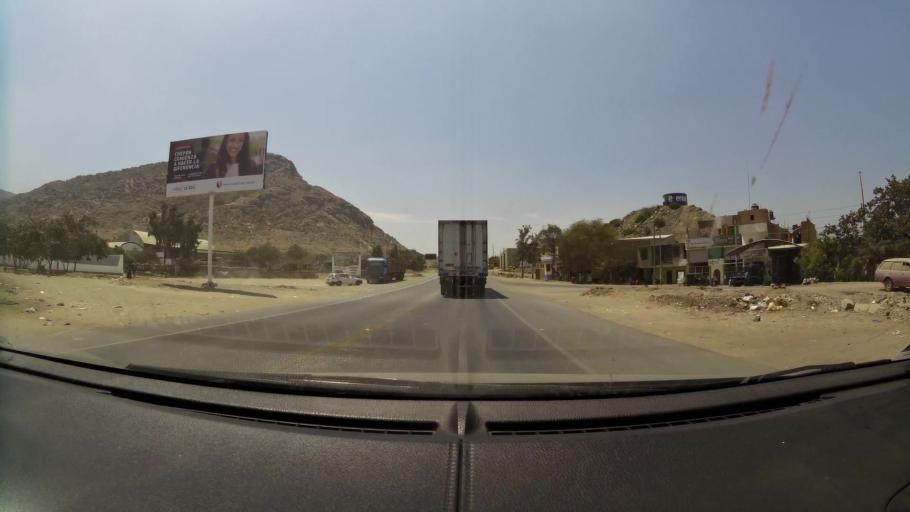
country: PE
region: La Libertad
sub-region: Provincia de Pacasmayo
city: Guadalupe
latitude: -7.3026
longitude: -79.4778
